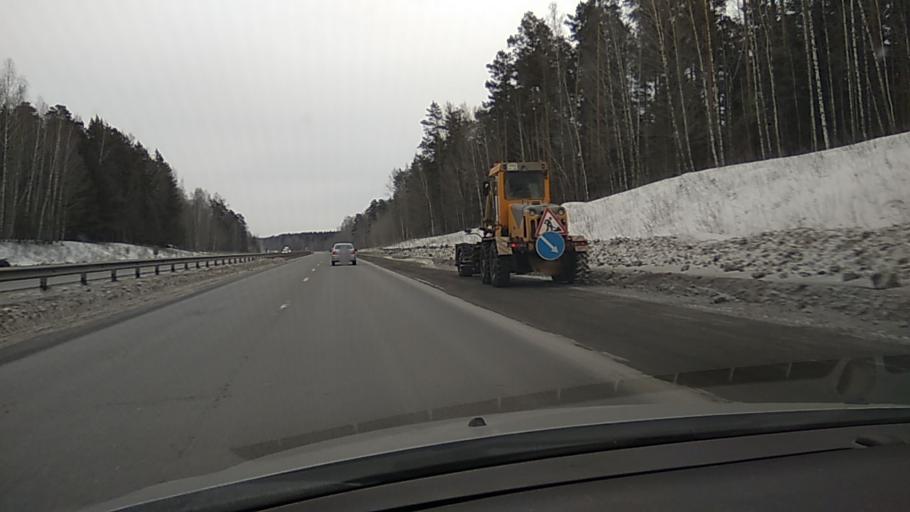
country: RU
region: Sverdlovsk
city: Talitsa
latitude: 56.8422
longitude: 60.0985
